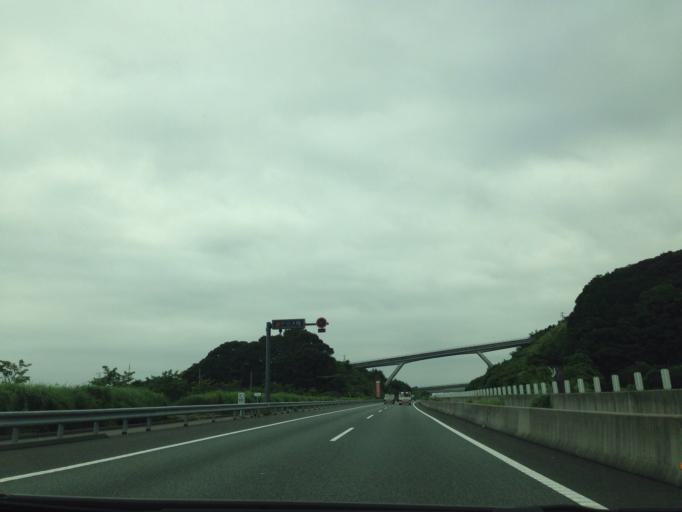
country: JP
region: Shizuoka
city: Fuji
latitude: 35.1754
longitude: 138.7392
